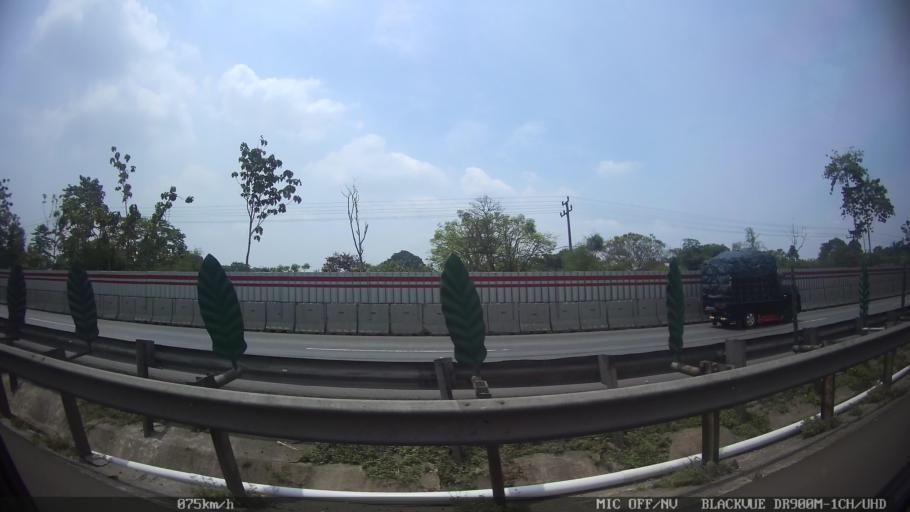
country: ID
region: West Java
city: Kresek
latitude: -6.1499
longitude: 106.3050
